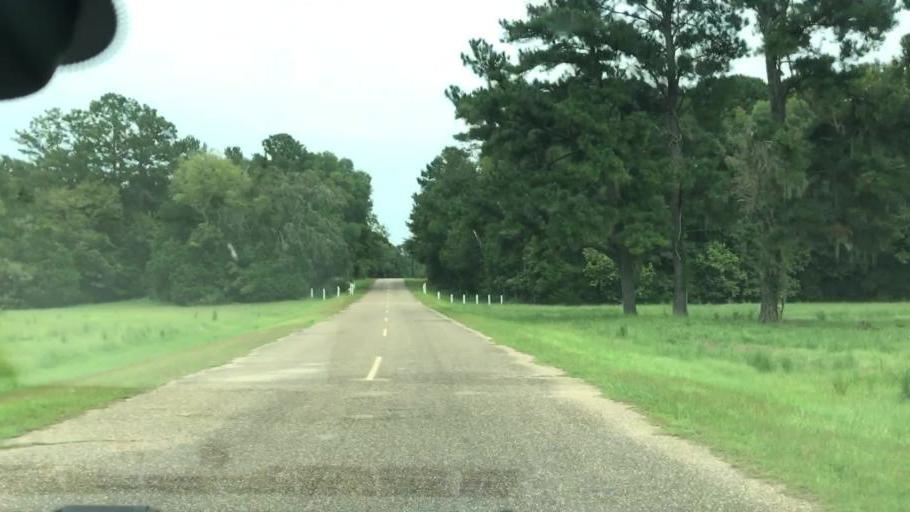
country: US
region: Georgia
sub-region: Clay County
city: Fort Gaines
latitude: 31.6270
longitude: -85.0551
